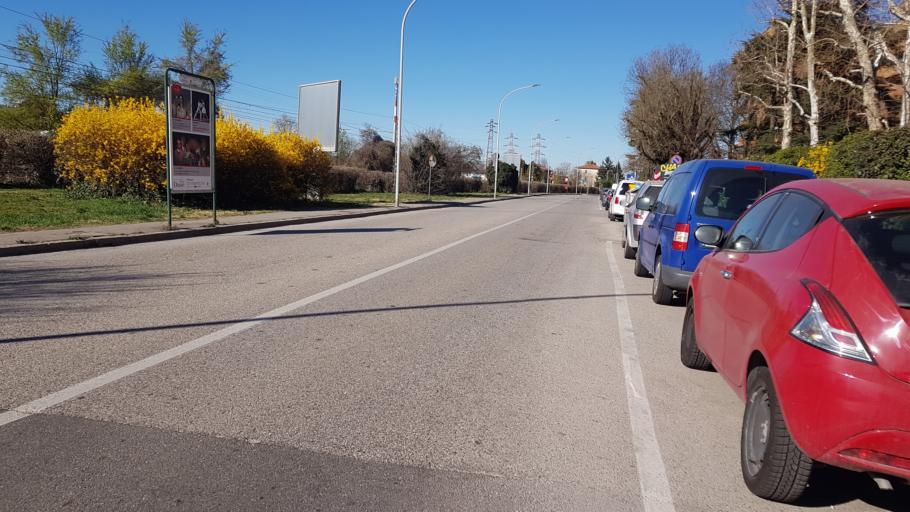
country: IT
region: Emilia-Romagna
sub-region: Provincia di Bologna
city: Bologna
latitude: 44.5197
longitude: 11.3246
